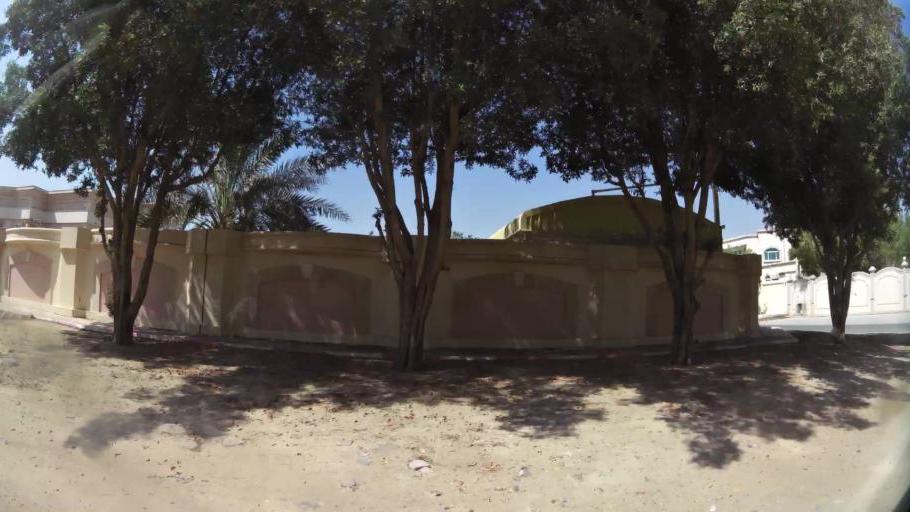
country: AE
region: Ajman
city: Ajman
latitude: 25.4081
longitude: 55.4796
